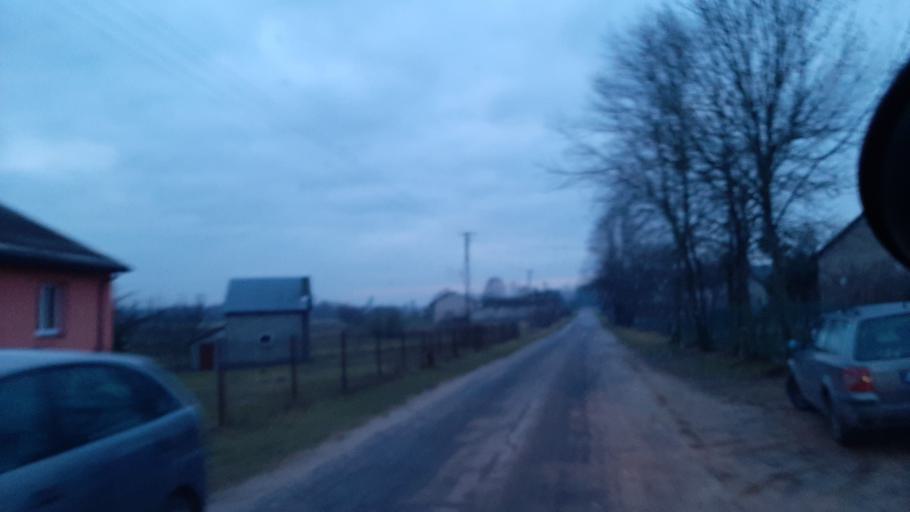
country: PL
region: Lublin Voivodeship
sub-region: Powiat lubartowski
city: Firlej
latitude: 51.5945
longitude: 22.5242
